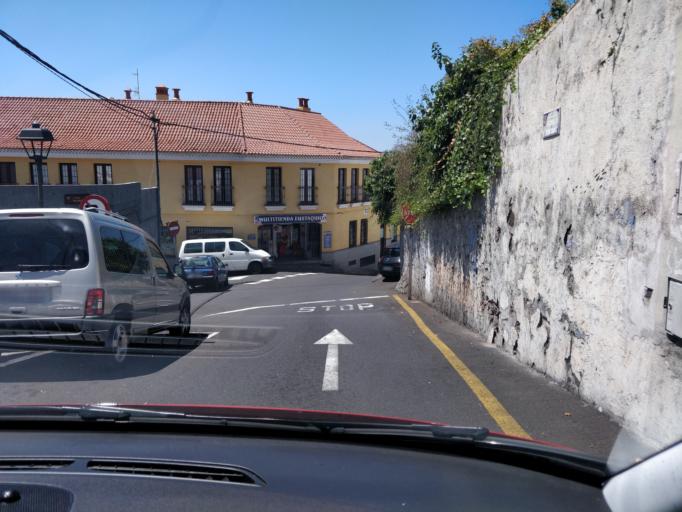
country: ES
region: Canary Islands
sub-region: Provincia de Santa Cruz de Tenerife
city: La Orotava
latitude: 28.3861
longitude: -16.5227
